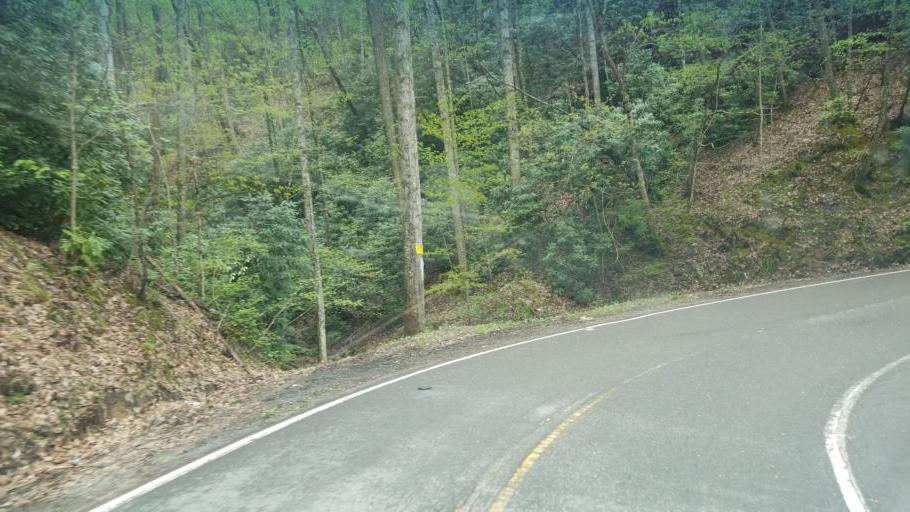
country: US
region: Virginia
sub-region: Tazewell County
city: Tazewell
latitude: 37.0054
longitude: -81.5171
